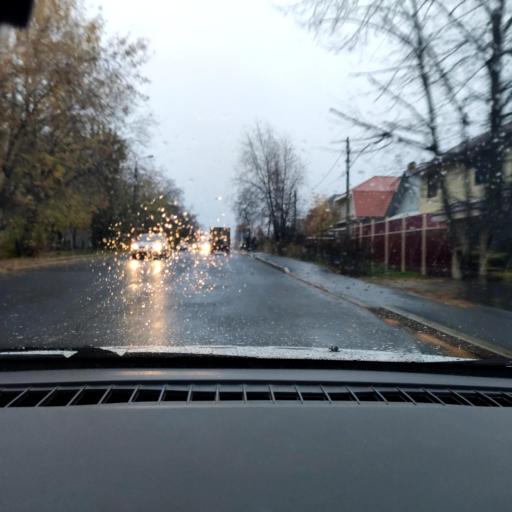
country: RU
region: Perm
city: Kondratovo
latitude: 58.0472
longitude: 56.0871
